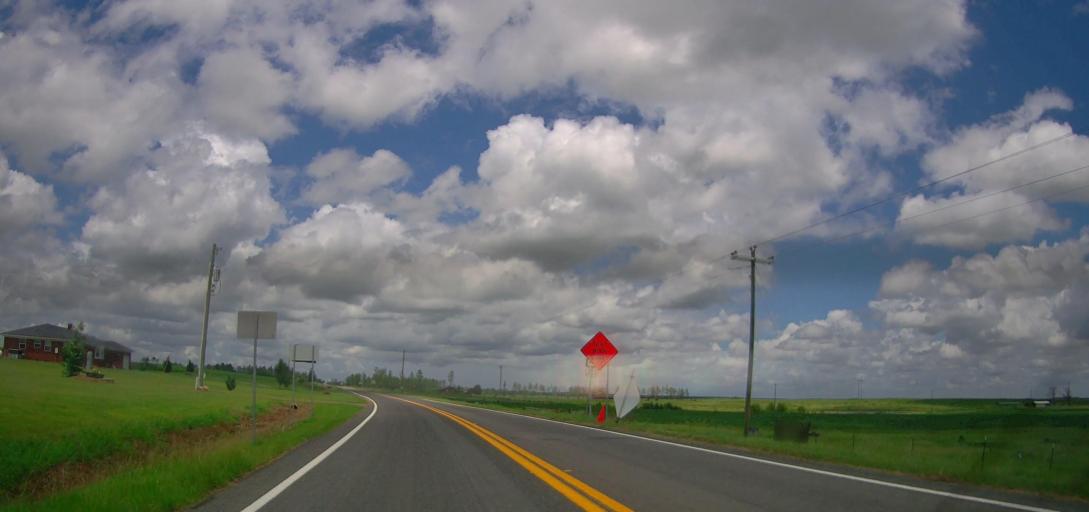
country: US
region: Georgia
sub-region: Turner County
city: Ashburn
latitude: 31.8223
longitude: -83.5643
